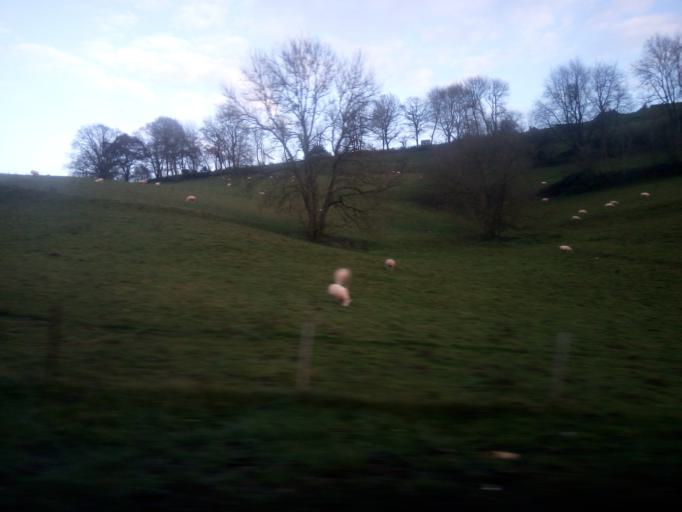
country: LU
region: Diekirch
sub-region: Canton de Vianden
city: Tandel
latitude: 49.9097
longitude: 6.1914
